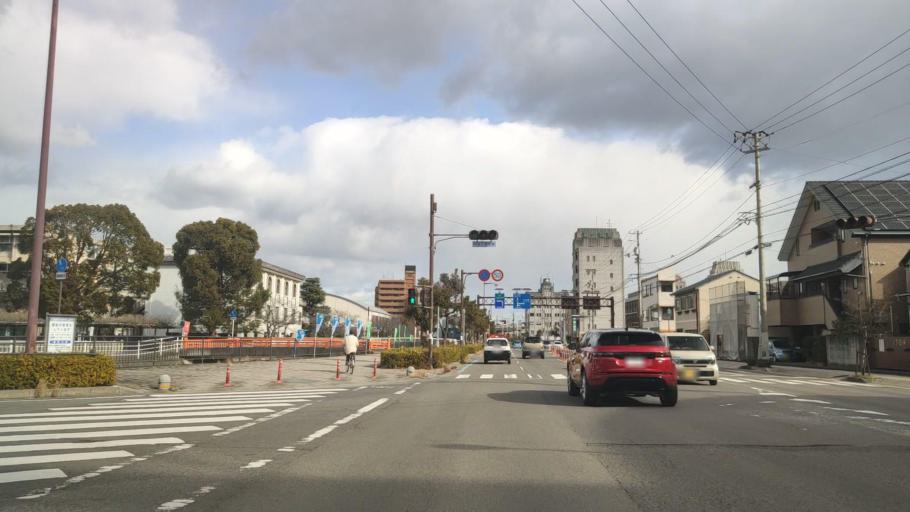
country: JP
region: Ehime
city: Hojo
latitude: 34.0639
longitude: 132.9882
